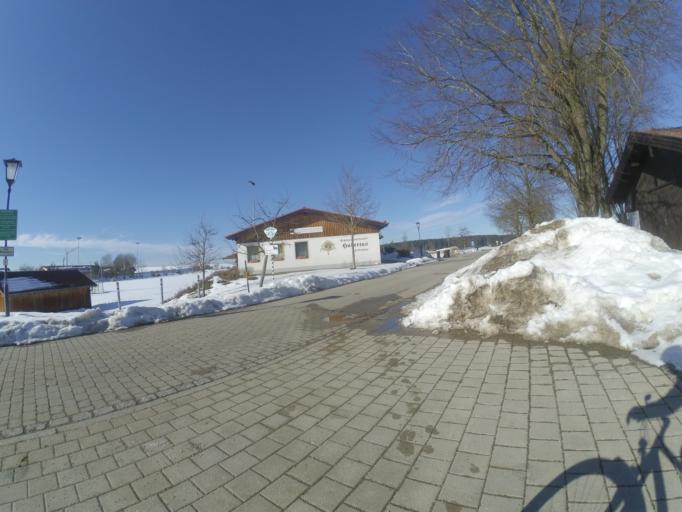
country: DE
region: Bavaria
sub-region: Upper Bavaria
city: Aying
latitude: 47.9462
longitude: 11.7939
